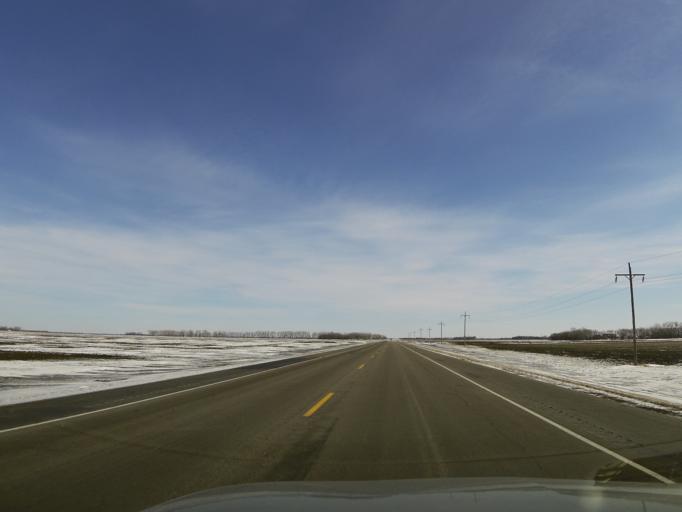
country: US
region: North Dakota
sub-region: Walsh County
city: Grafton
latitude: 48.4120
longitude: -97.2437
